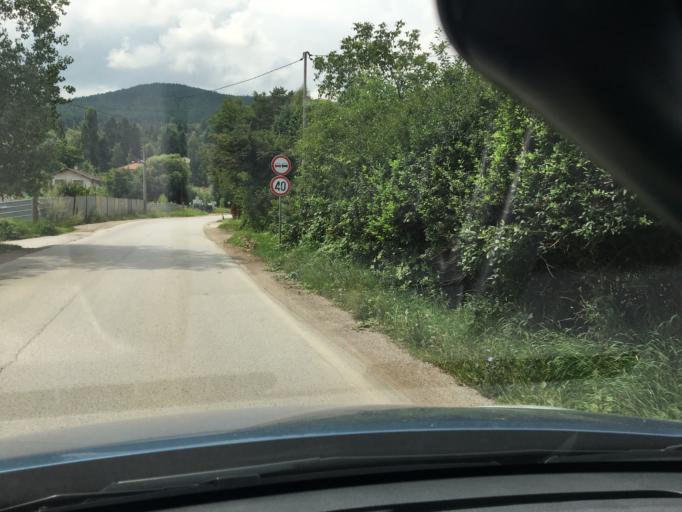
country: BG
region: Sofia-Capital
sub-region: Stolichna Obshtina
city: Sofia
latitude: 42.6123
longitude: 23.3638
